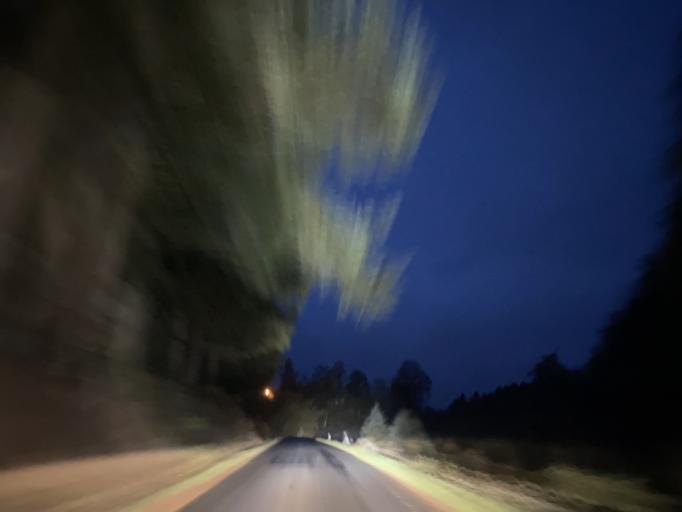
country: FR
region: Auvergne
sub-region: Departement du Puy-de-Dome
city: Montaigut
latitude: 45.5985
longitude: 3.5028
